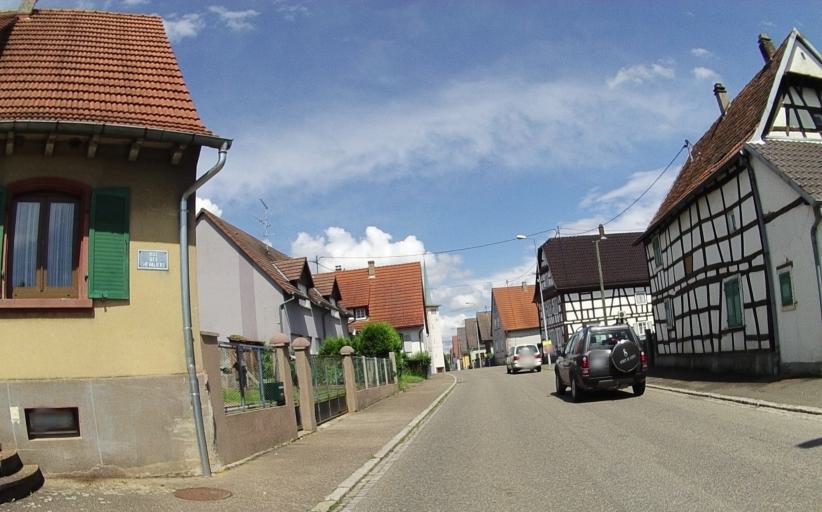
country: FR
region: Alsace
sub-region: Departement du Bas-Rhin
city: Betschdorf
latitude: 48.9016
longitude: 7.9509
